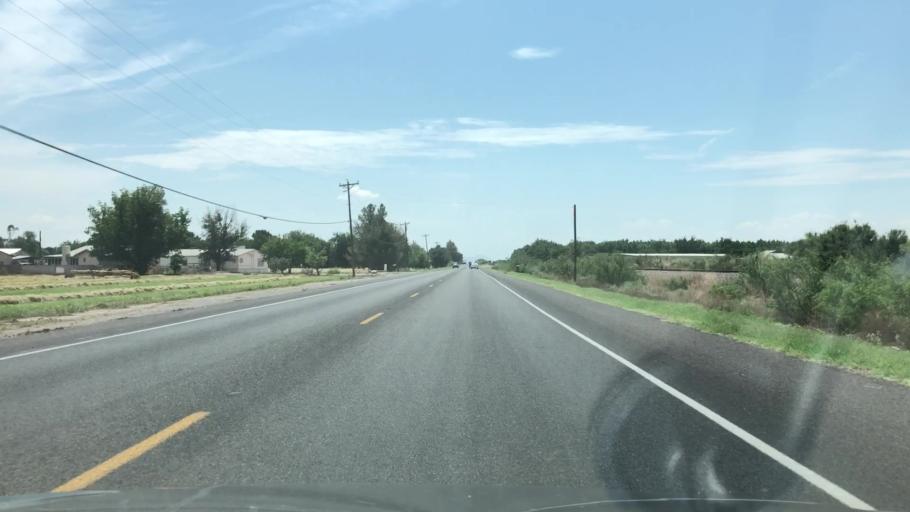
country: US
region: New Mexico
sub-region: Dona Ana County
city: Mesquite
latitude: 32.2071
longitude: -106.7235
